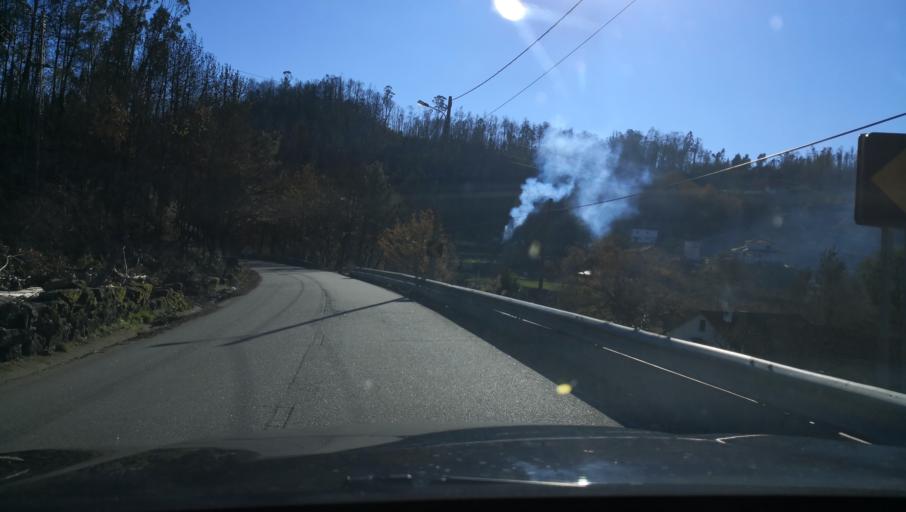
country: PT
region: Viseu
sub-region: Oliveira de Frades
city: Oliveira de Frades
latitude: 40.7309
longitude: -8.1508
